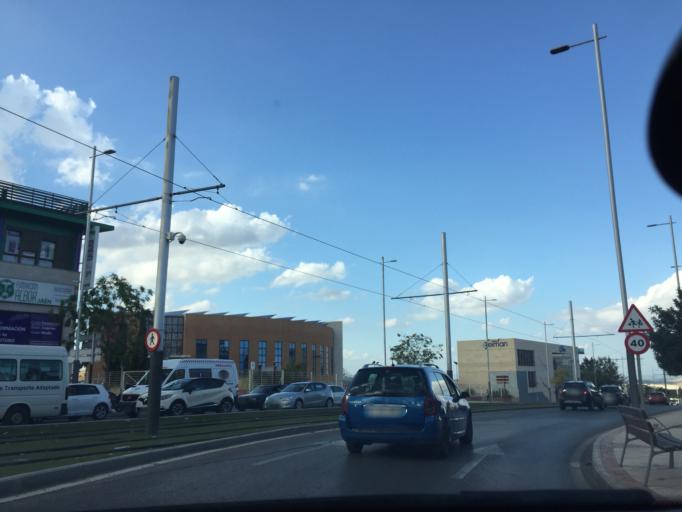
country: ES
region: Andalusia
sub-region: Provincia de Jaen
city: Jaen
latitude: 37.7839
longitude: -3.7838
